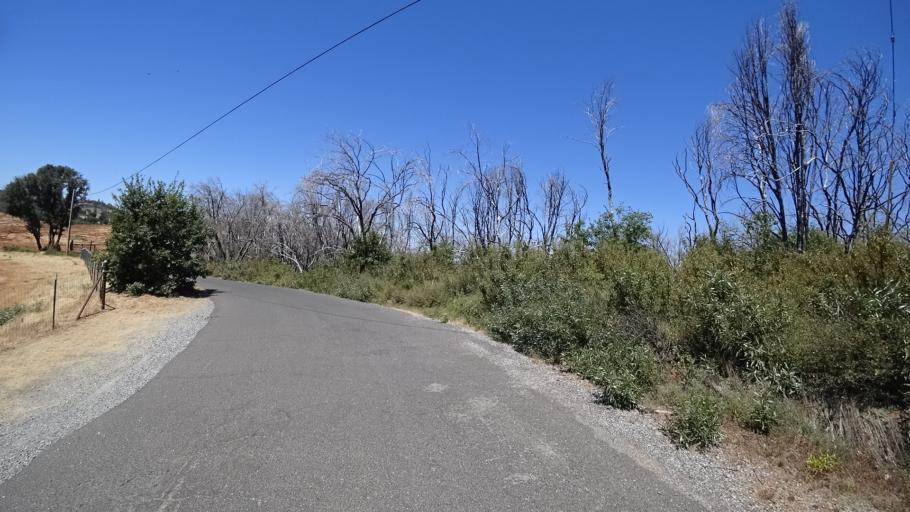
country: US
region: California
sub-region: Calaveras County
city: Mountain Ranch
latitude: 38.2297
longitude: -120.5936
